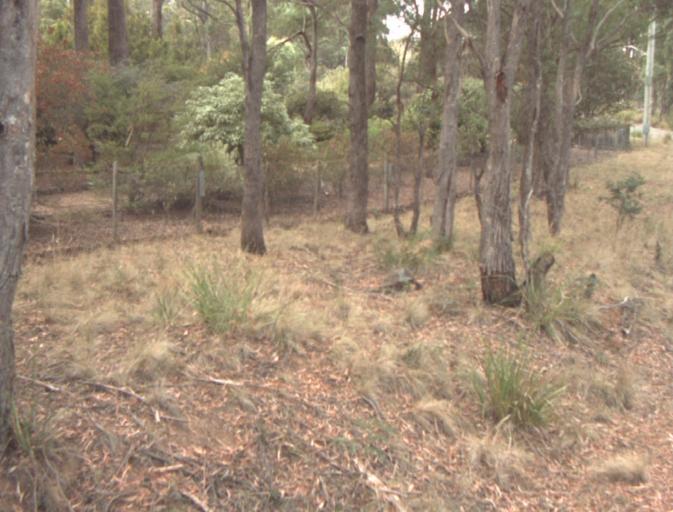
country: AU
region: Tasmania
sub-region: Launceston
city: Mayfield
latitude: -41.2788
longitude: 147.0545
